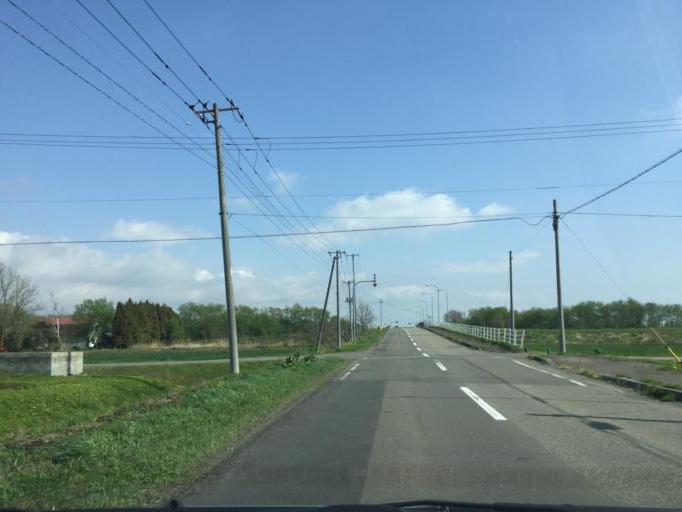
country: JP
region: Hokkaido
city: Iwamizawa
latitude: 43.1472
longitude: 141.7195
